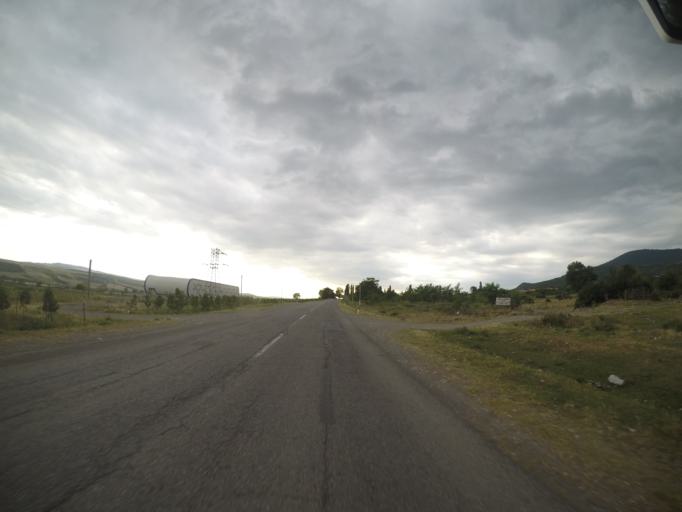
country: AZ
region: Ismayilli
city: Ismayilli
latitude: 40.7542
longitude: 48.2295
